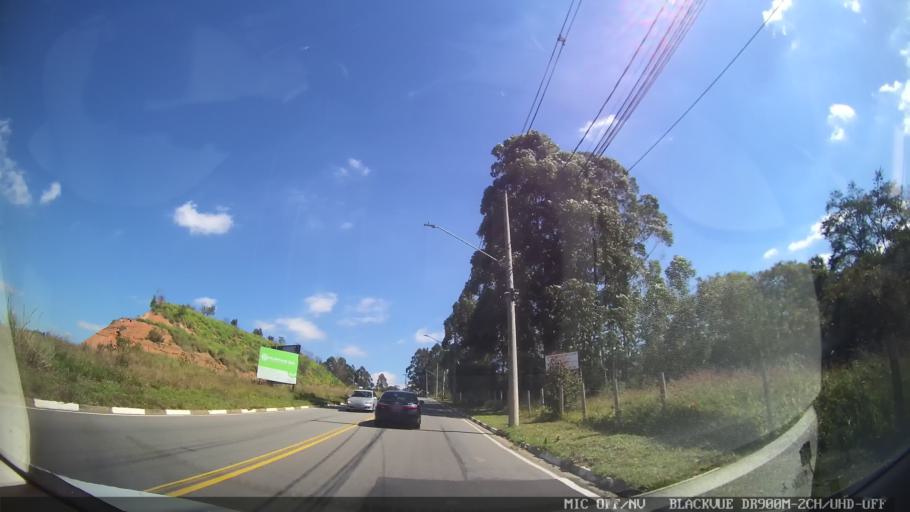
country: BR
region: Sao Paulo
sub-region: Barueri
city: Barueri
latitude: -23.4441
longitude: -46.8349
